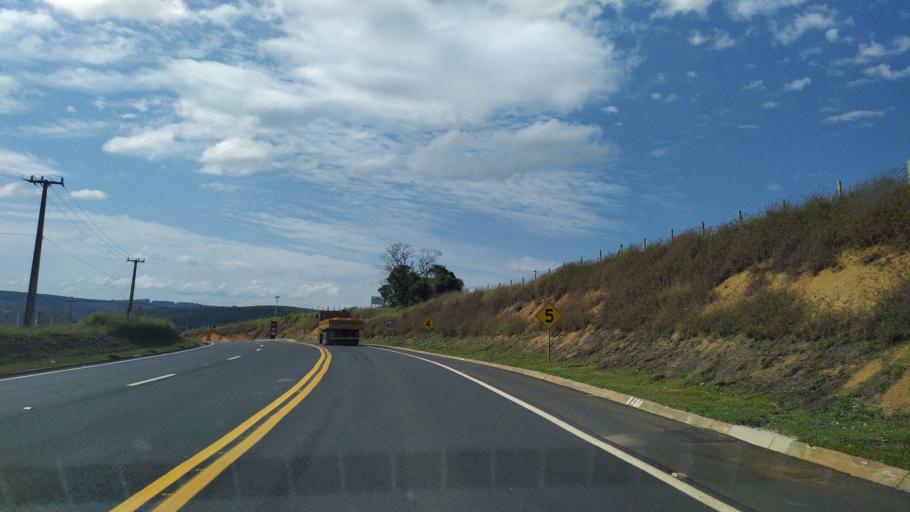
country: BR
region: Parana
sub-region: Telemaco Borba
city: Telemaco Borba
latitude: -24.2859
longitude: -50.7084
